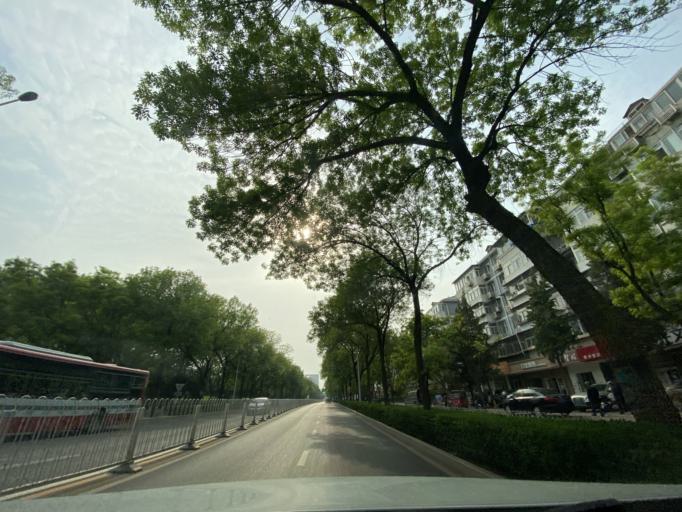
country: CN
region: Beijing
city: Qinghe
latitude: 39.9753
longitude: 116.3589
